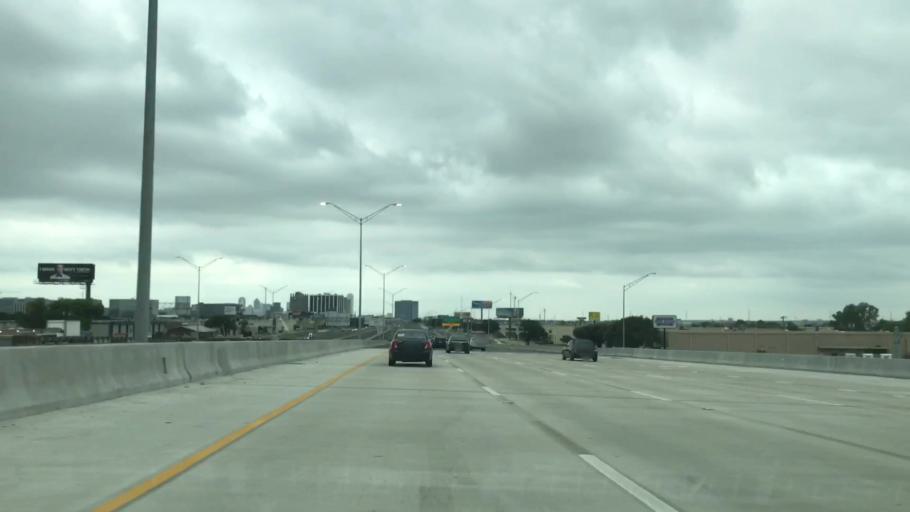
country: US
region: Texas
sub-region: Dallas County
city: Irving
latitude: 32.8275
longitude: -96.8862
